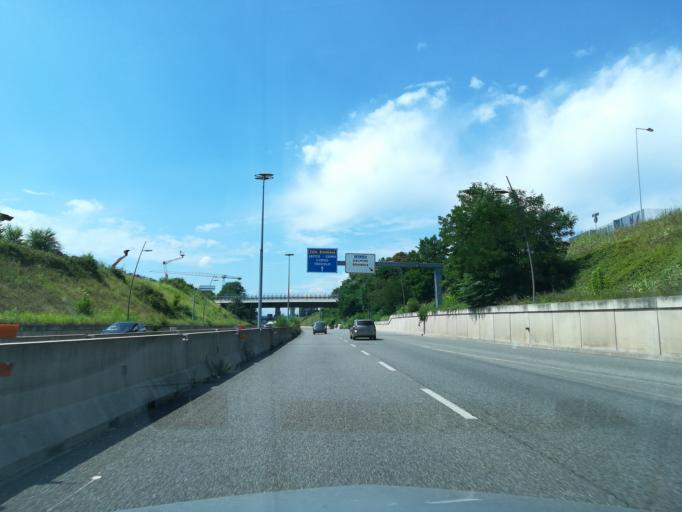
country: IT
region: Lombardy
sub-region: Provincia di Bergamo
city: Lallio
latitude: 45.6531
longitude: 9.6192
